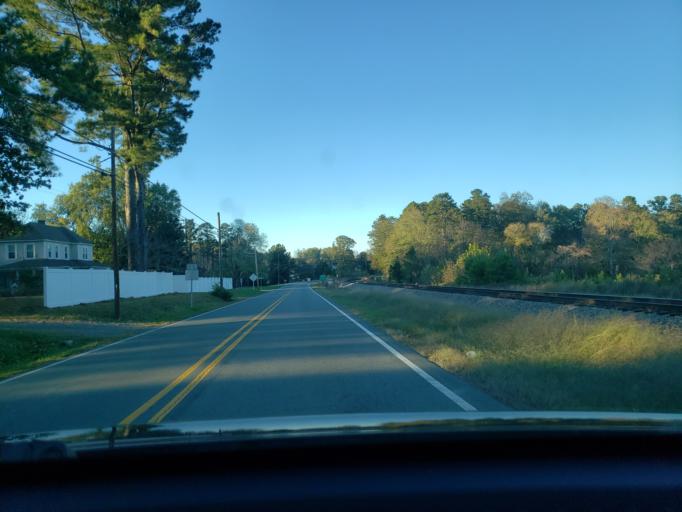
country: US
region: North Carolina
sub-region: Forsyth County
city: Walkertown
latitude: 36.2232
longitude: -80.1688
